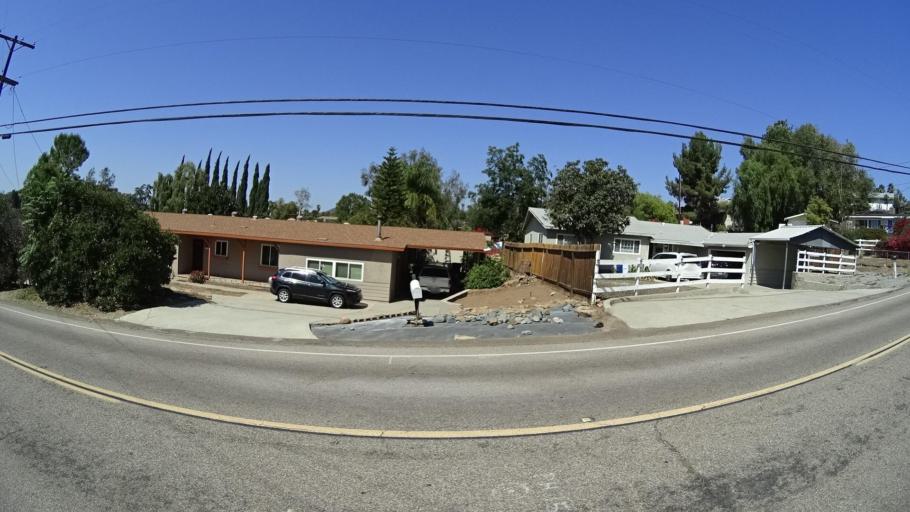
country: US
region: California
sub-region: San Diego County
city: Granite Hills
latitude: 32.8083
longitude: -116.9089
